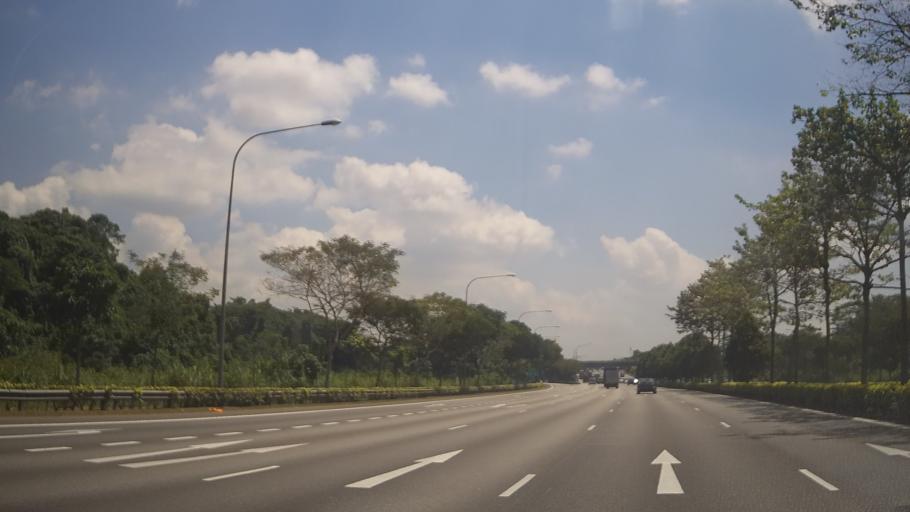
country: MY
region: Johor
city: Kampung Pasir Gudang Baru
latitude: 1.3933
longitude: 103.8286
